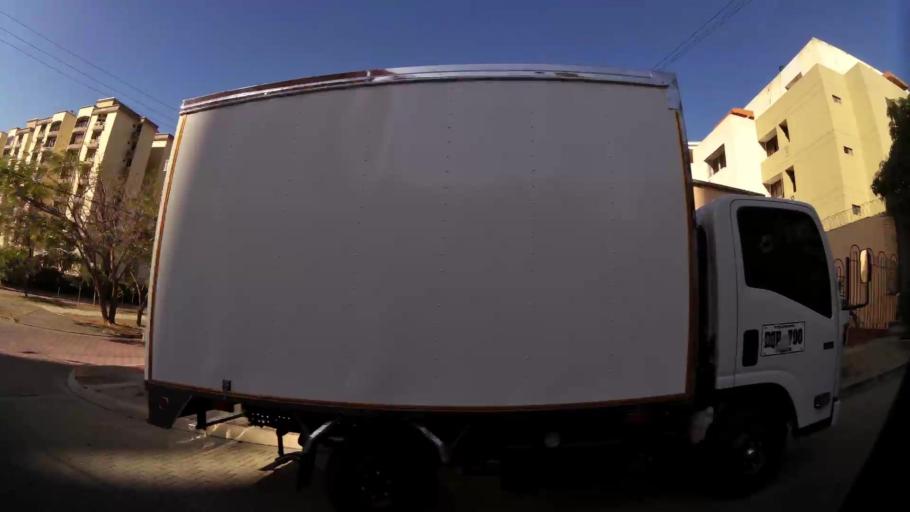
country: CO
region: Atlantico
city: Barranquilla
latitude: 11.0052
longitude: -74.8301
